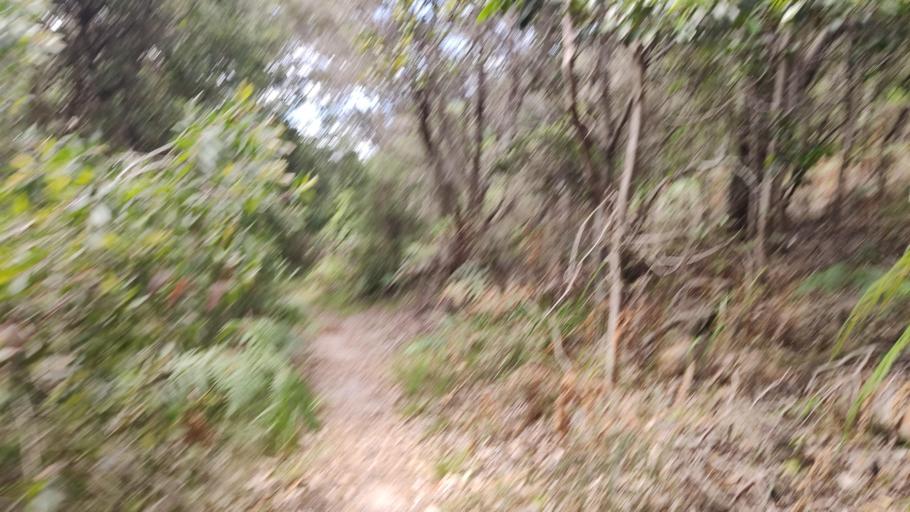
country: AU
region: New South Wales
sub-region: Port Macquarie-Hastings
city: North Haven
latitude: -31.6434
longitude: 152.8413
